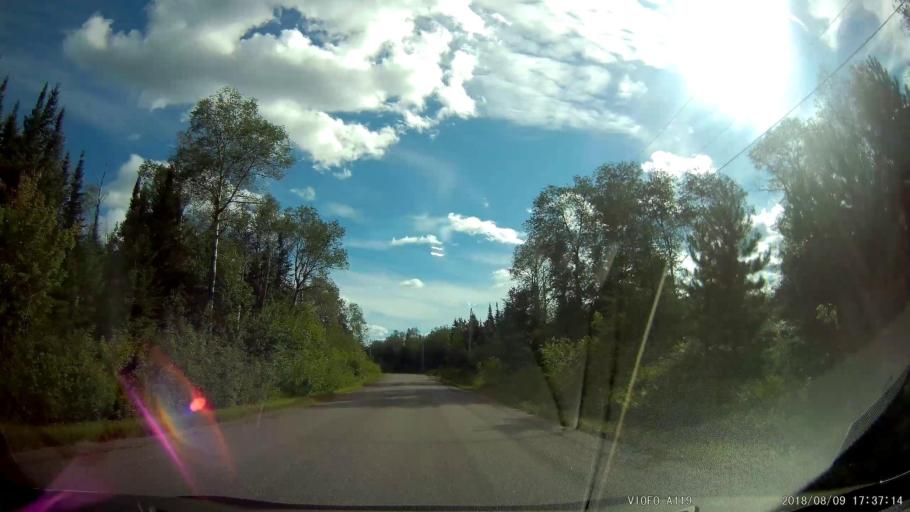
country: CA
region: Ontario
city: Rayside-Balfour
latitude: 46.6109
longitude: -81.4729
